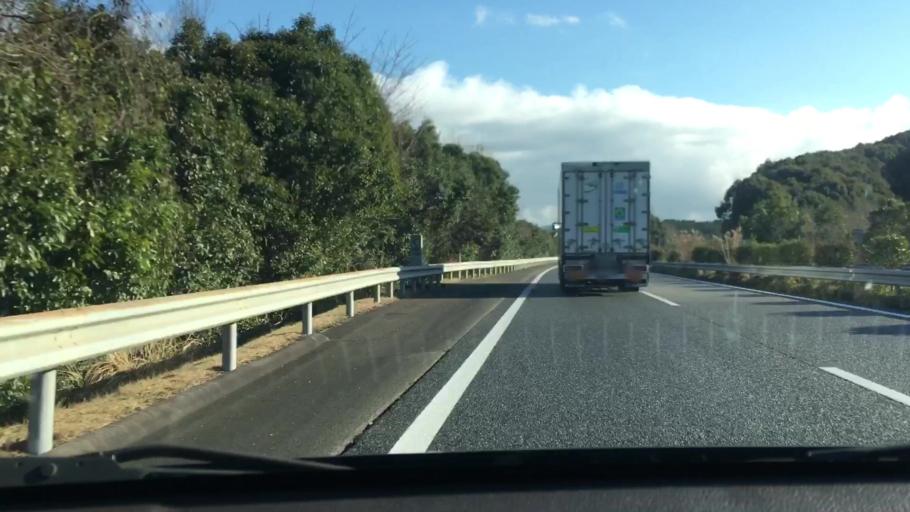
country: JP
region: Kumamoto
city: Hitoyoshi
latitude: 32.1705
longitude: 130.7918
